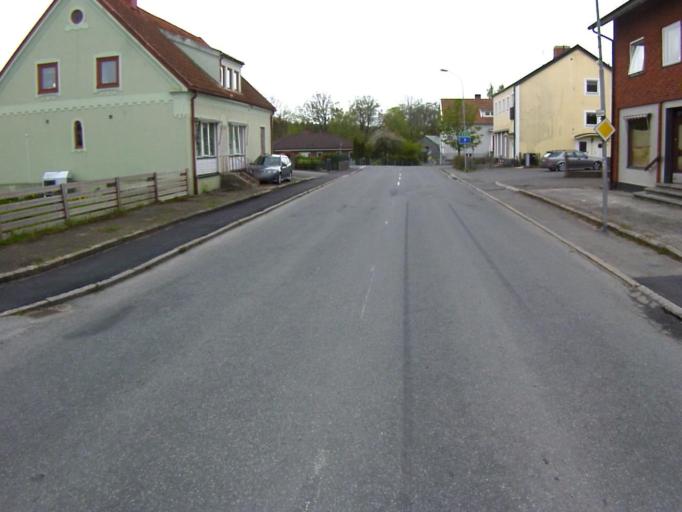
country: SE
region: Skane
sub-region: Kristianstads Kommun
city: Onnestad
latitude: 55.9320
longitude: 13.9728
